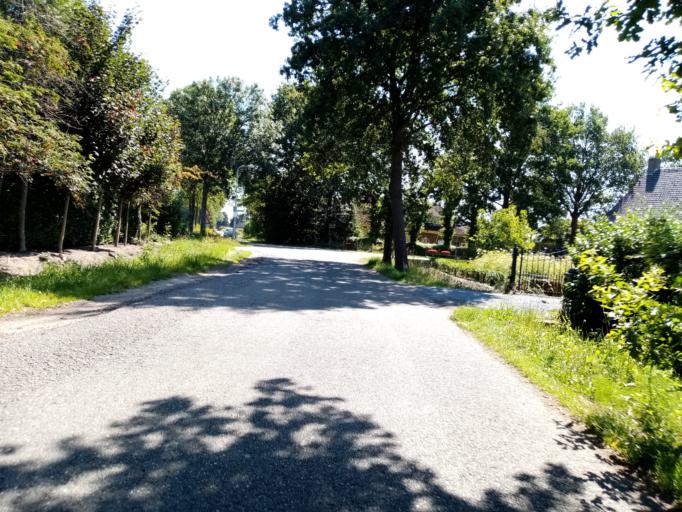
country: NL
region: North Brabant
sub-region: Gemeente Breda
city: Breda
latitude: 51.6250
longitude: 4.7118
